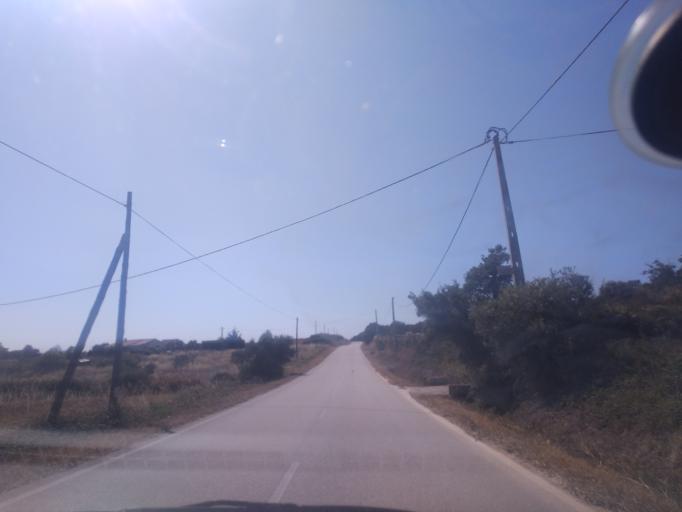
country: PT
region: Faro
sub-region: Aljezur
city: Aljezur
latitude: 37.2240
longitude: -8.8089
